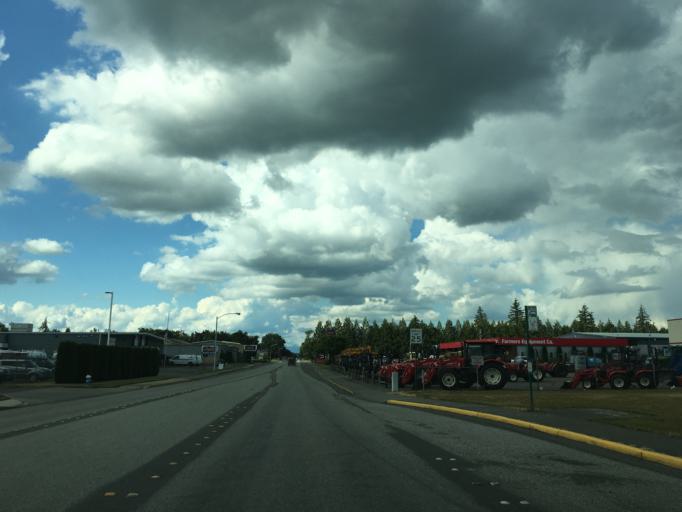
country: US
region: Washington
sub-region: Whatcom County
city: Lynden
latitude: 48.9403
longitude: -122.4809
